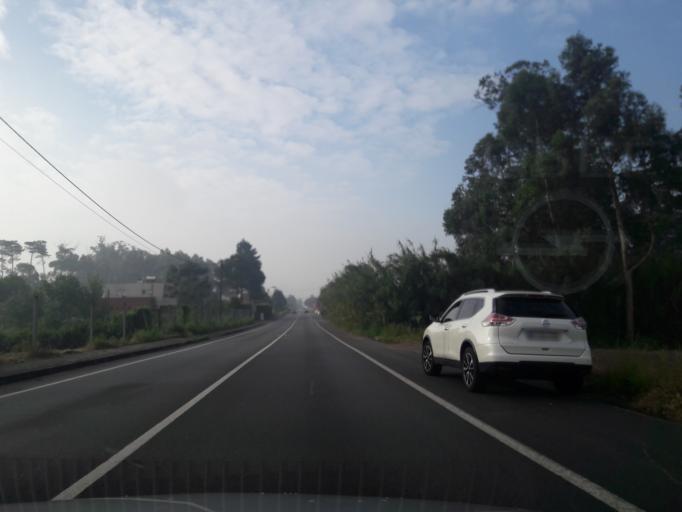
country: PT
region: Porto
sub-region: Vila do Conde
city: Arvore
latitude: 41.3146
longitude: -8.7087
